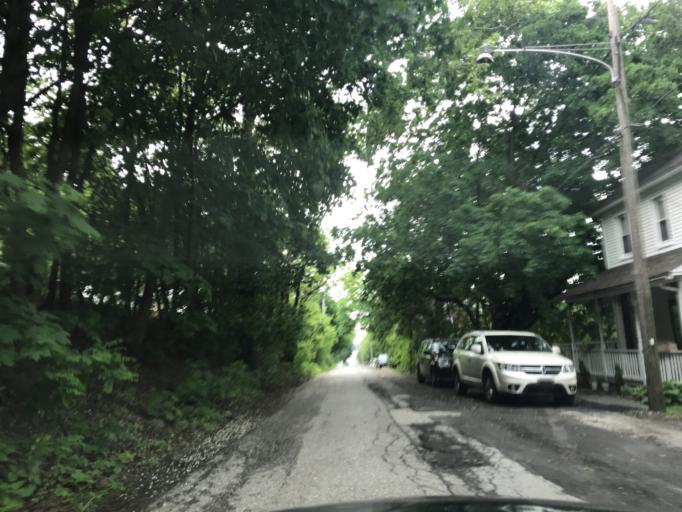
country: US
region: Pennsylvania
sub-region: York County
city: Susquehanna Trails
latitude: 39.7288
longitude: -76.3197
